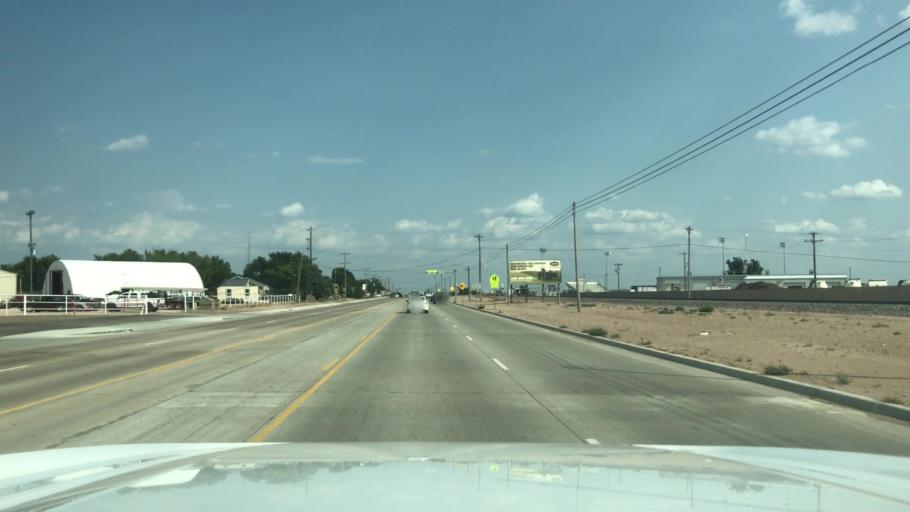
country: US
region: Texas
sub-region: Dallam County
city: Dalhart
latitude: 36.0531
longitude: -102.5040
